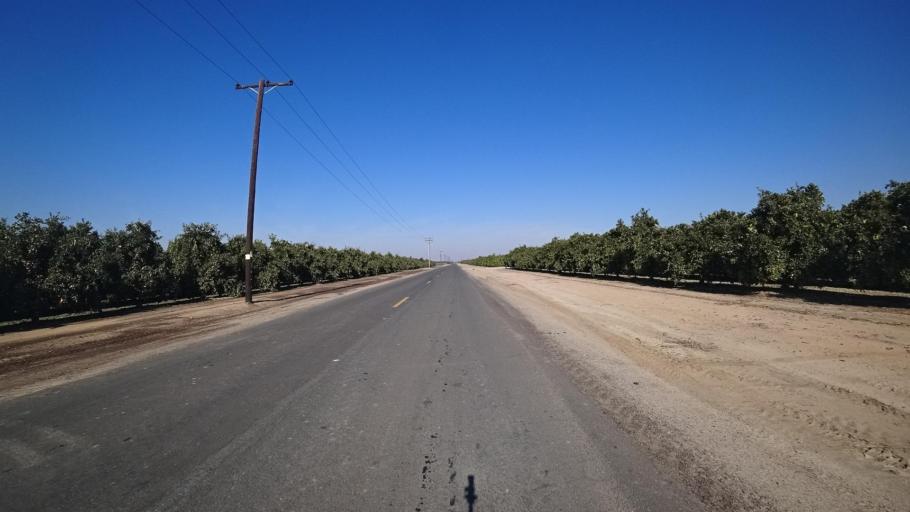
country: US
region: California
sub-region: Tulare County
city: Richgrove
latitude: 35.7262
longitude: -119.1340
